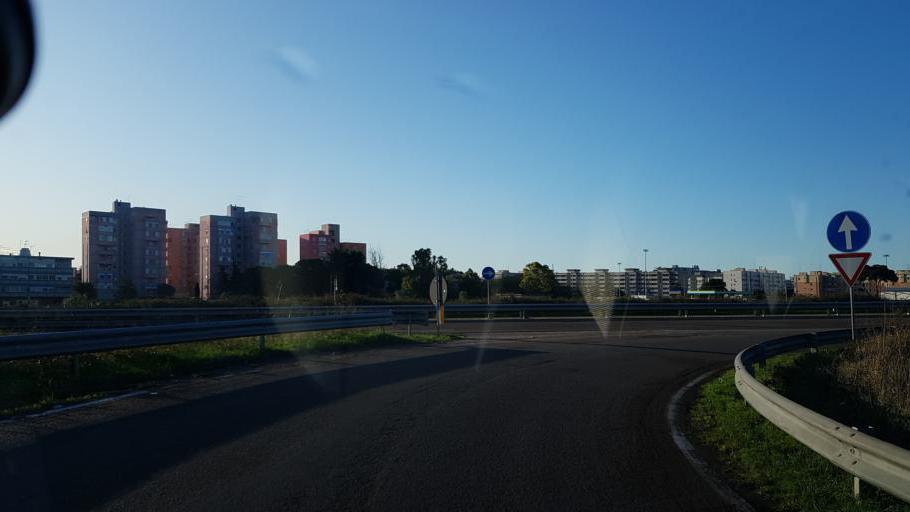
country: IT
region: Apulia
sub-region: Provincia di Brindisi
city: Brindisi
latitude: 40.6263
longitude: 17.9502
